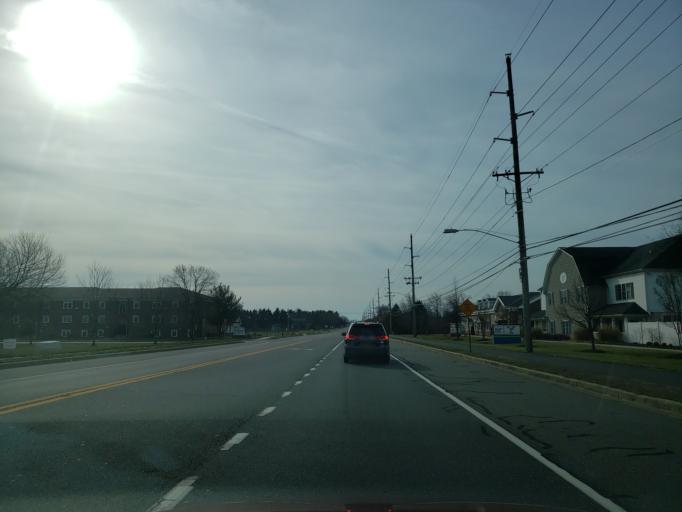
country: US
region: Delaware
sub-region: Kent County
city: Dover
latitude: 39.1680
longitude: -75.5461
